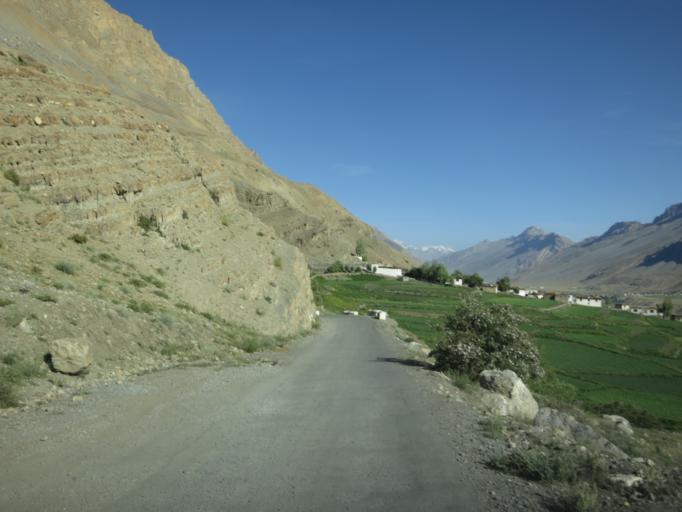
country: IN
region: Himachal Pradesh
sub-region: Shimla
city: Sarahan
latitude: 32.2952
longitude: 78.0098
